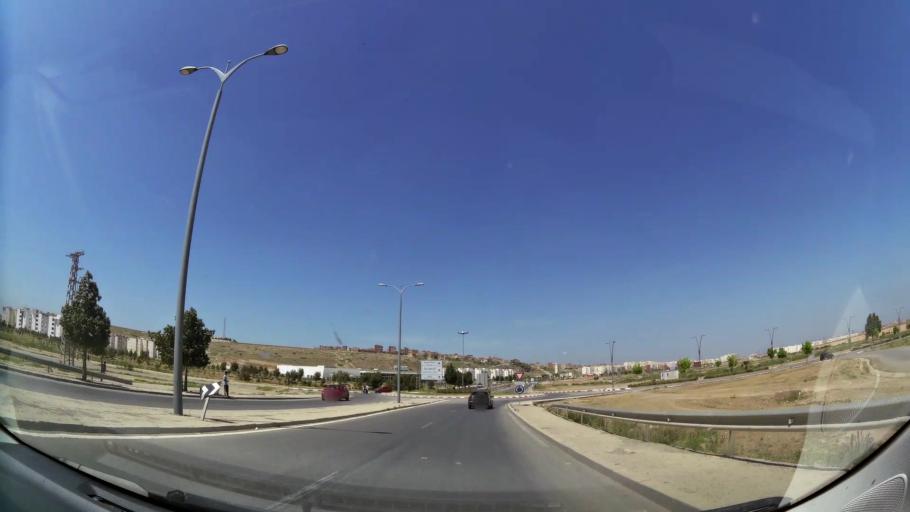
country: MA
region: Oriental
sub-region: Oujda-Angad
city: Oujda
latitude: 34.6962
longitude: -1.9411
